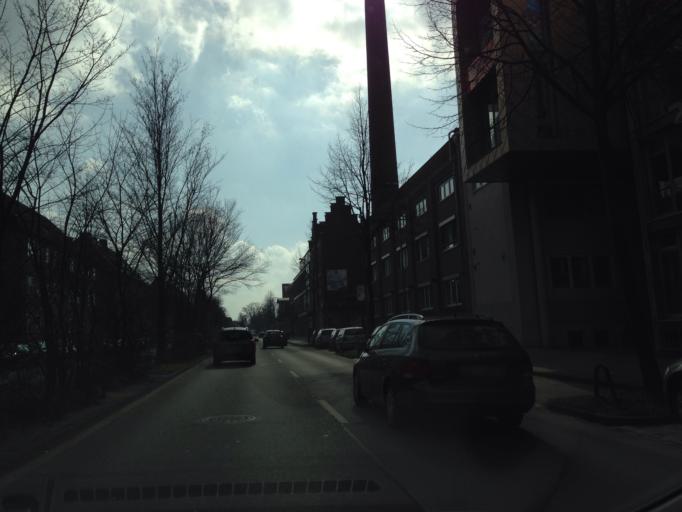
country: DE
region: North Rhine-Westphalia
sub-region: Regierungsbezirk Munster
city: Muenster
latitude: 51.9783
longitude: 7.6121
